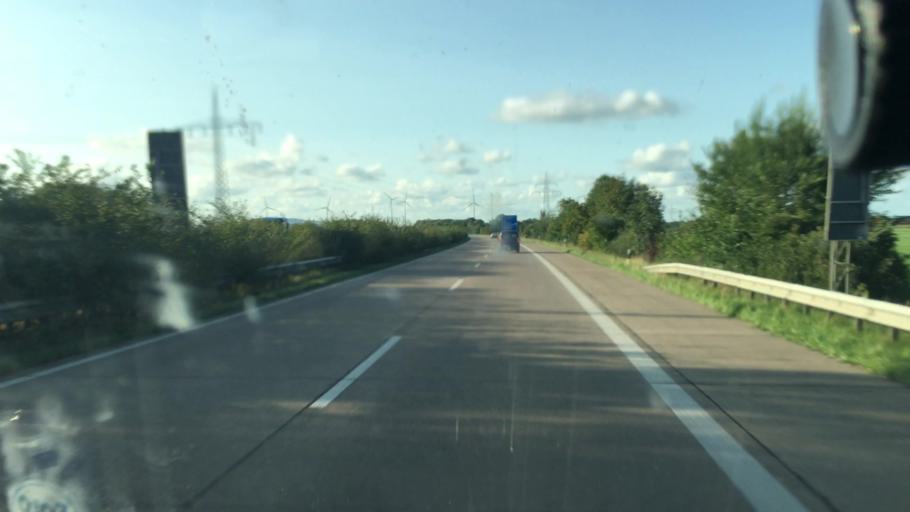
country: DE
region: Lower Saxony
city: Sande
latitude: 53.4771
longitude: 8.0134
